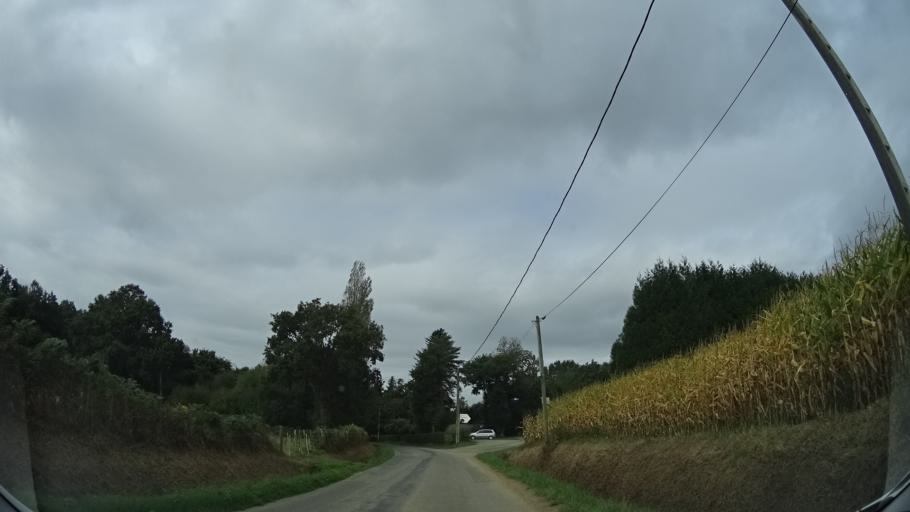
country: FR
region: Brittany
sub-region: Departement d'Ille-et-Vilaine
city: Irodouer
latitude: 48.2846
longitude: -1.8963
